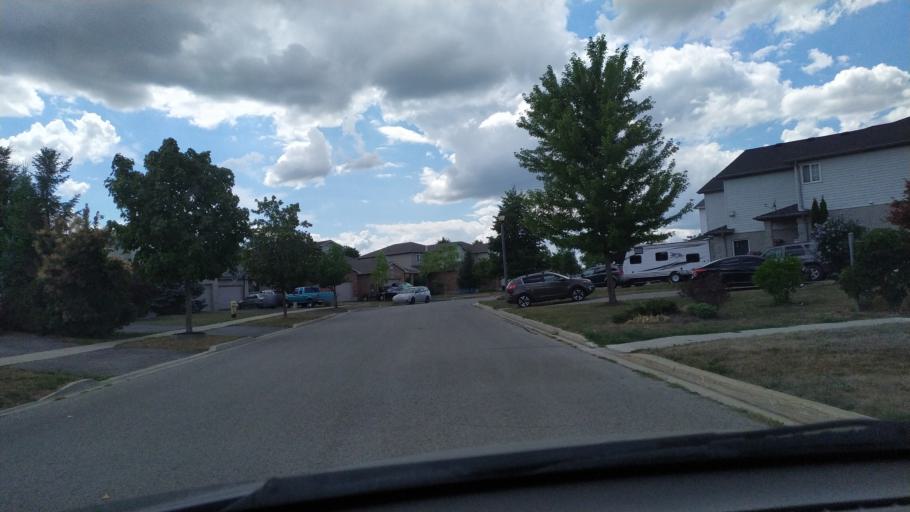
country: CA
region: Ontario
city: Stratford
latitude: 43.3776
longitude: -81.0008
